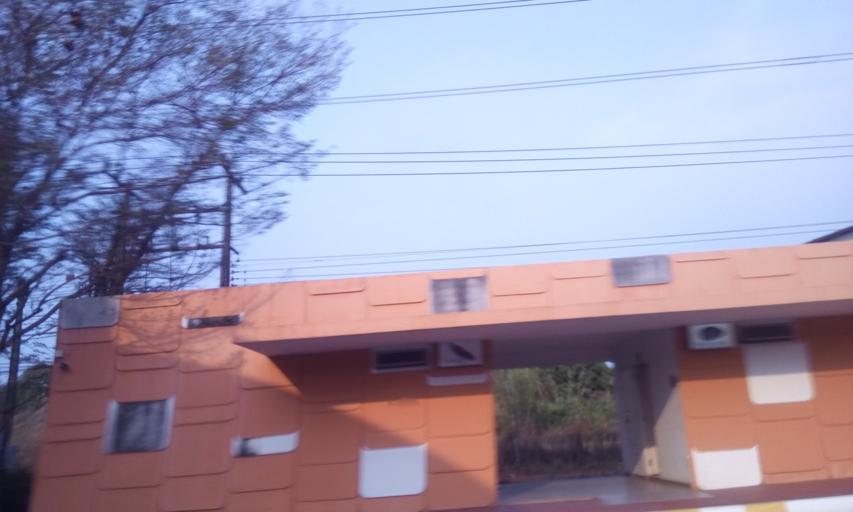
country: TH
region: Trat
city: Khao Saming
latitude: 12.3828
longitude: 102.3730
